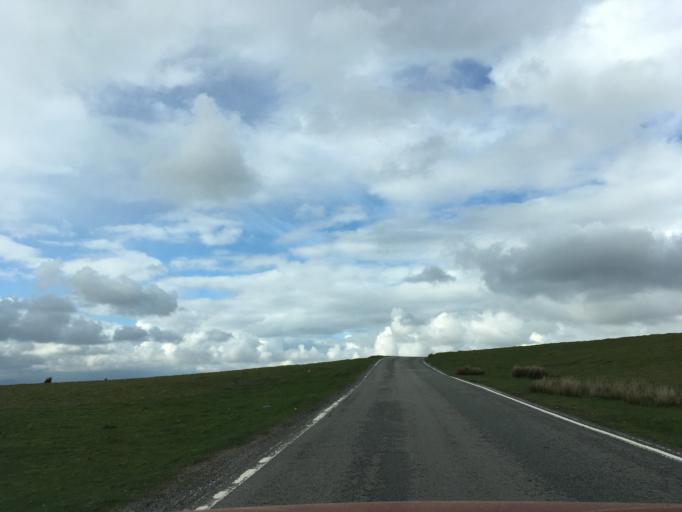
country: GB
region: Wales
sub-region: Caerphilly County Borough
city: Rhymney
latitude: 51.7170
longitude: -3.3076
